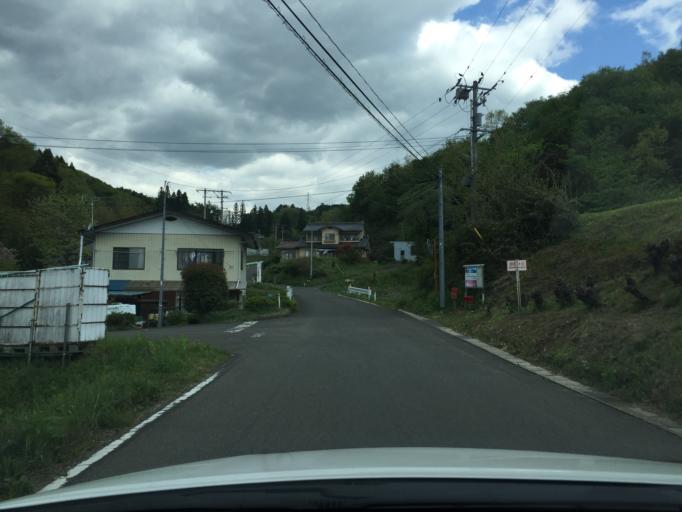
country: JP
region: Fukushima
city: Fukushima-shi
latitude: 37.7046
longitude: 140.5555
